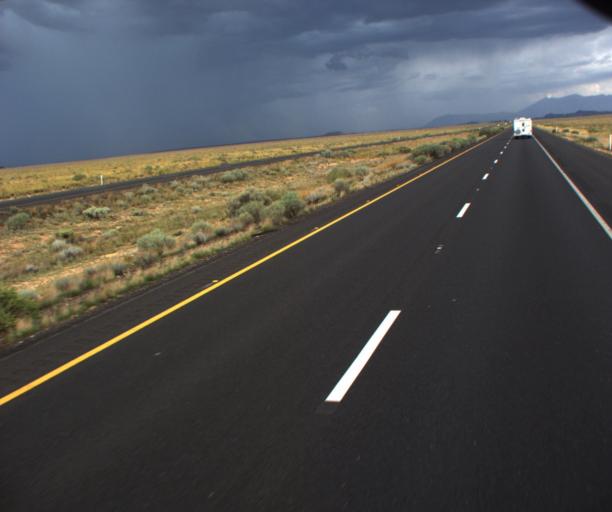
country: US
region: Arizona
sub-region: Coconino County
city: Flagstaff
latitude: 35.1441
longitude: -111.2242
